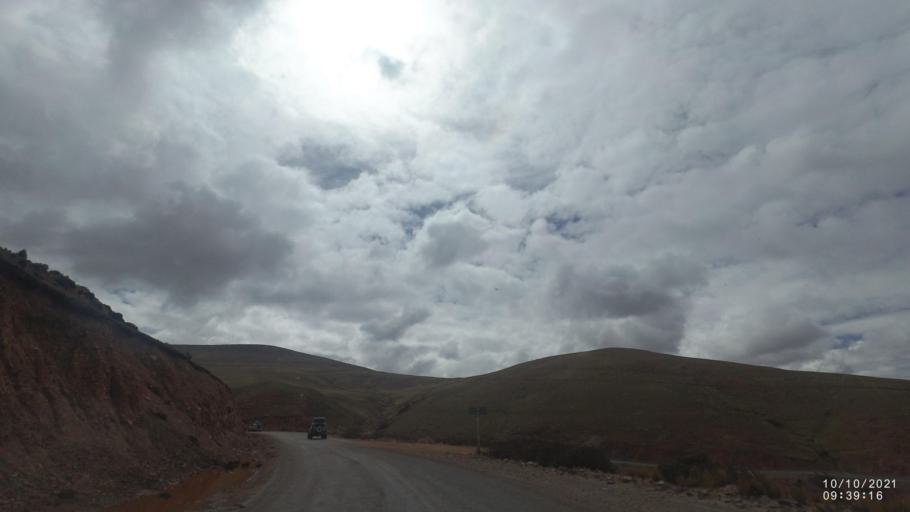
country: BO
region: La Paz
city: Quime
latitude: -17.1372
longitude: -67.3418
